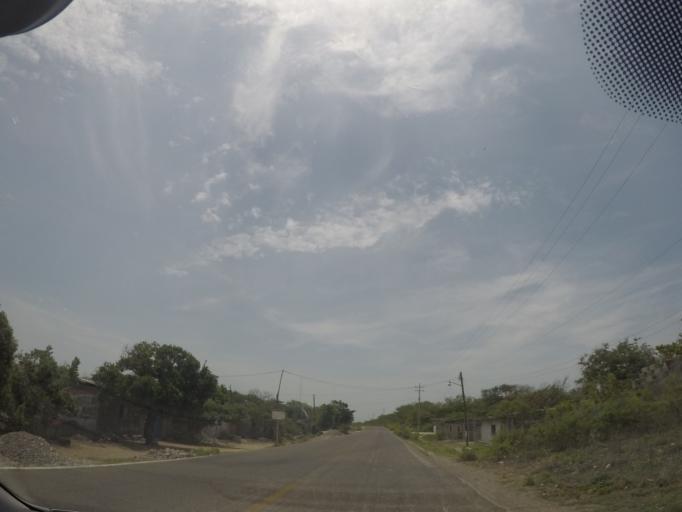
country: MX
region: Oaxaca
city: San Mateo del Mar
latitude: 16.2082
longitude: -95.0010
